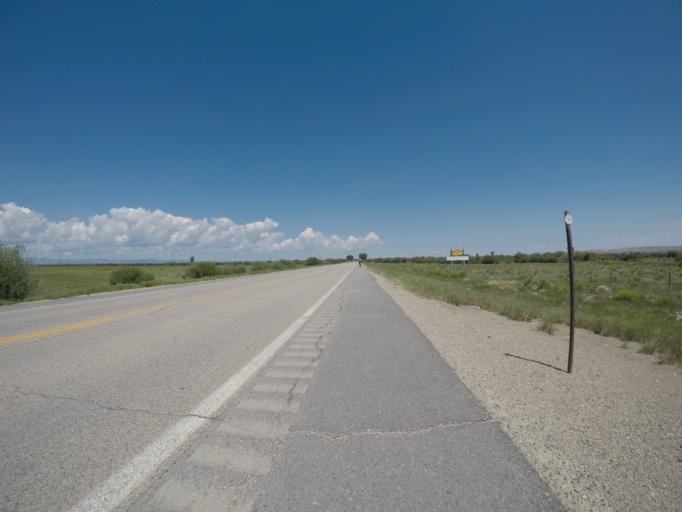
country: US
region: Wyoming
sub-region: Sublette County
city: Marbleton
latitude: 42.5191
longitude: -110.1057
